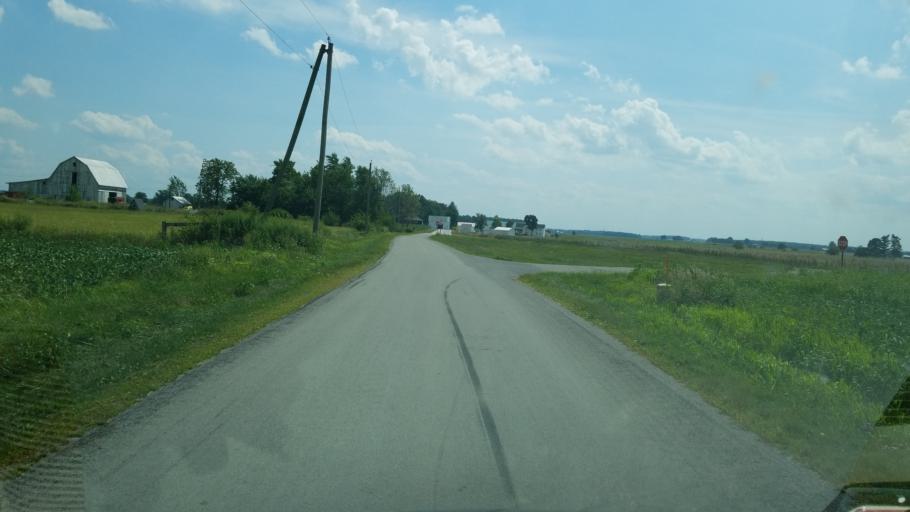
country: US
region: Ohio
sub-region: Hardin County
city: Forest
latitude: 40.7819
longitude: -83.4679
